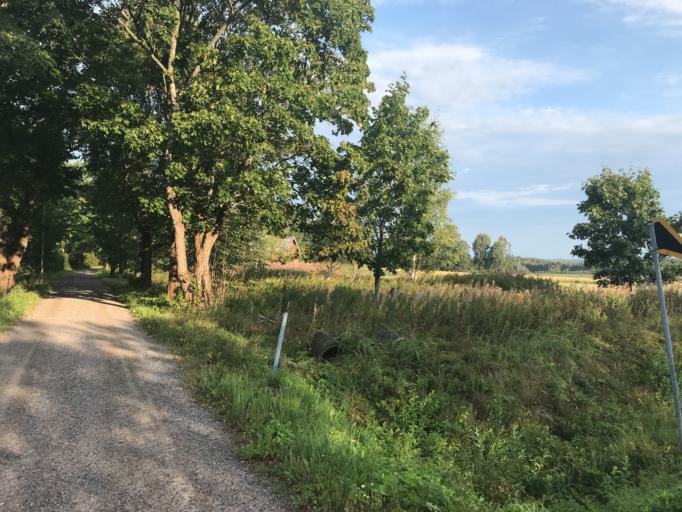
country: FI
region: Uusimaa
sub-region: Helsinki
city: Vihti
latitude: 60.4471
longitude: 24.5403
